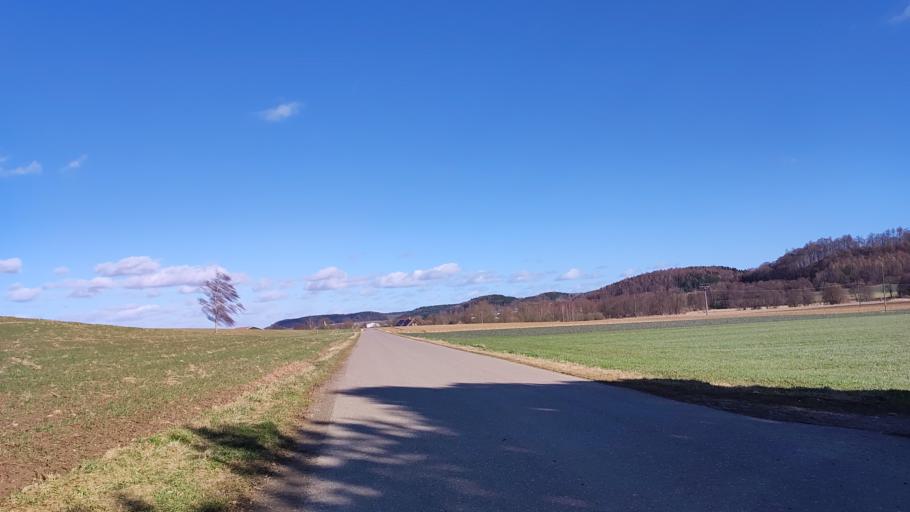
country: DE
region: Bavaria
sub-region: Swabia
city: Zusmarshausen
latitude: 48.4202
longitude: 10.5905
